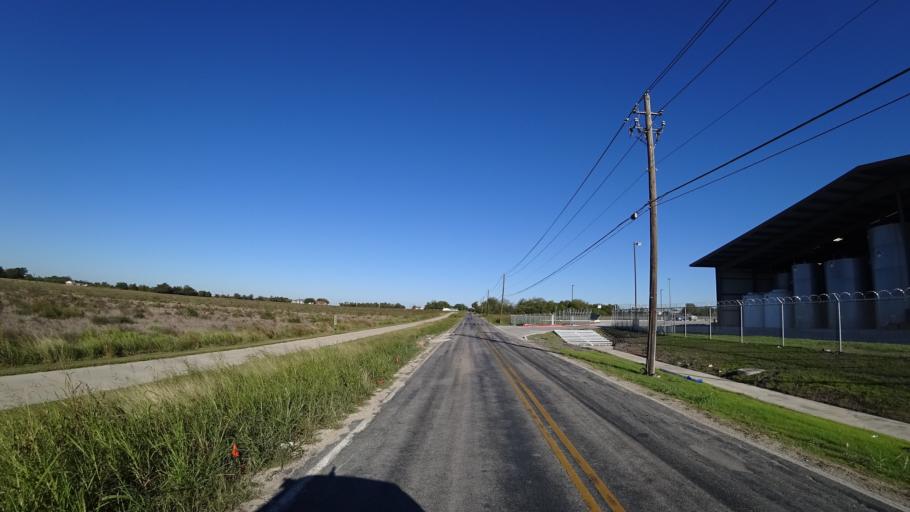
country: US
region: Texas
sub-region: Travis County
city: Manor
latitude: 30.3241
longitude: -97.6312
